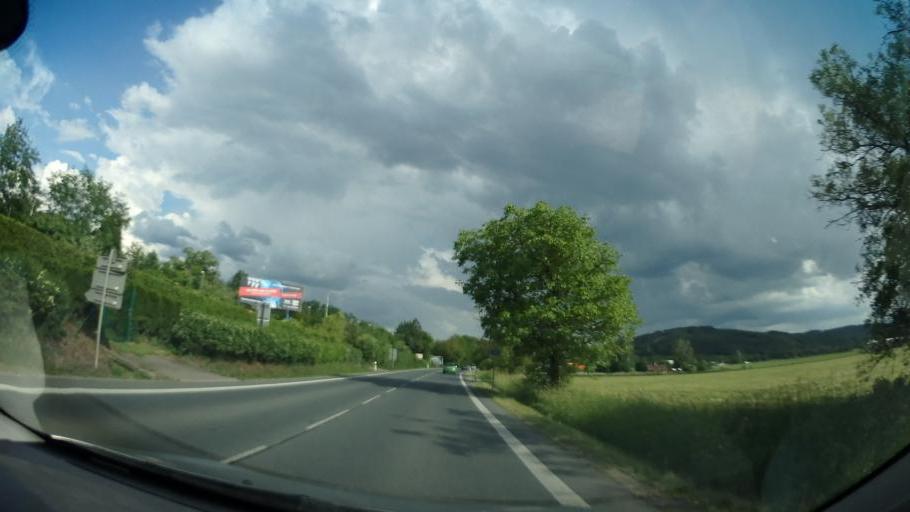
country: CZ
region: South Moravian
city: Tisnov
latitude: 49.3353
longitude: 16.4355
